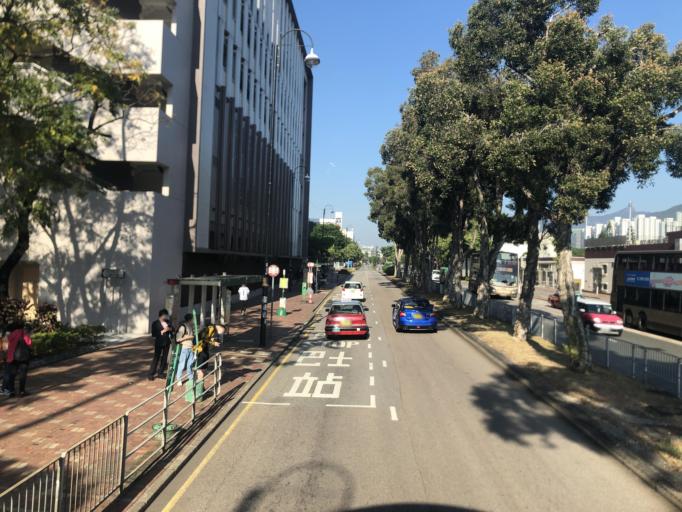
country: HK
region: Sha Tin
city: Sha Tin
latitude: 22.3840
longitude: 114.1929
